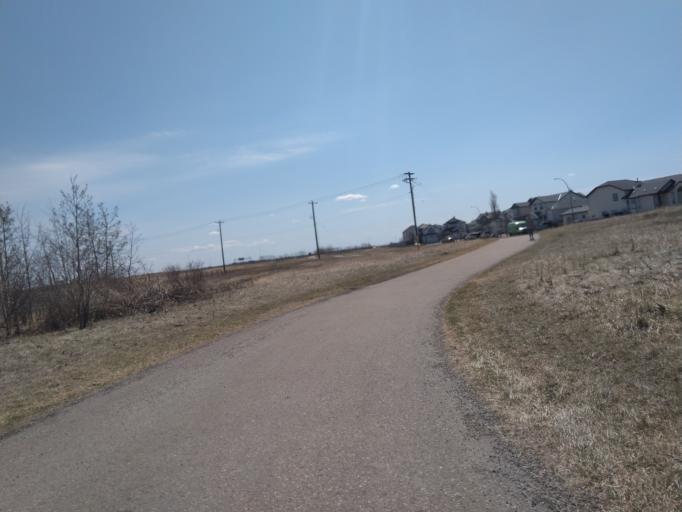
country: CA
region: Alberta
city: Chestermere
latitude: 51.0939
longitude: -113.9271
